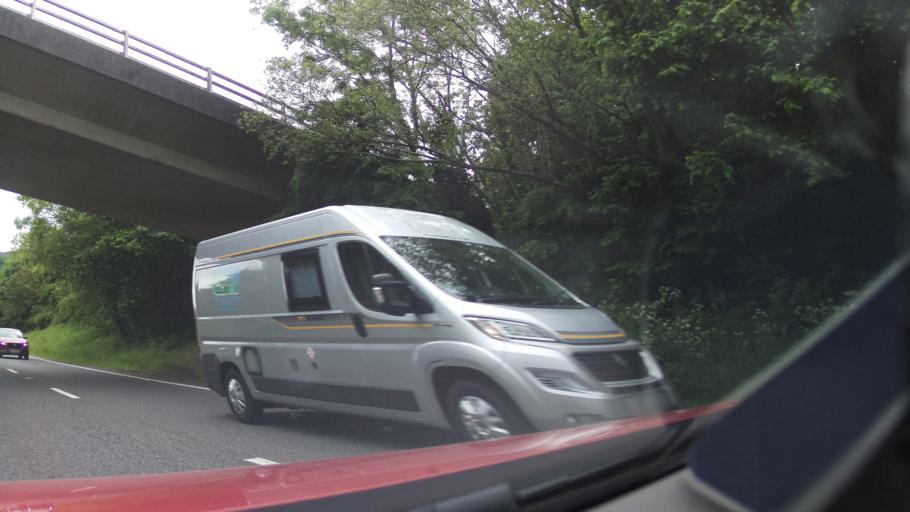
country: GB
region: England
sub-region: Dorset
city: Lyme Regis
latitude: 50.7414
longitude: -2.8951
